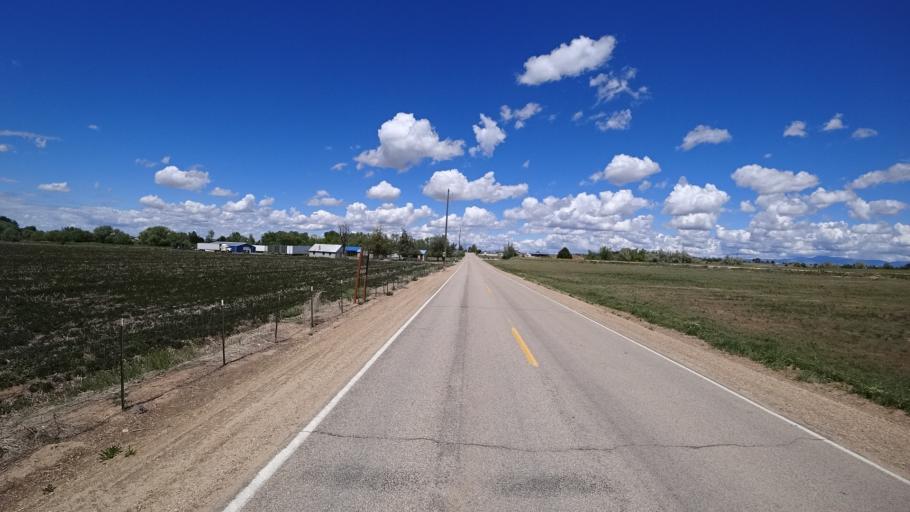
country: US
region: Idaho
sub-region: Ada County
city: Kuna
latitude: 43.5542
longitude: -116.4537
